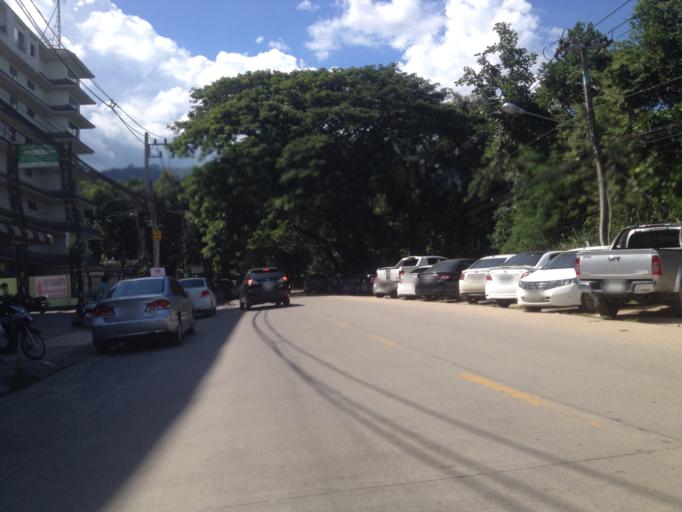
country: TH
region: Chiang Mai
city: Chiang Mai
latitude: 18.7935
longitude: 98.9526
